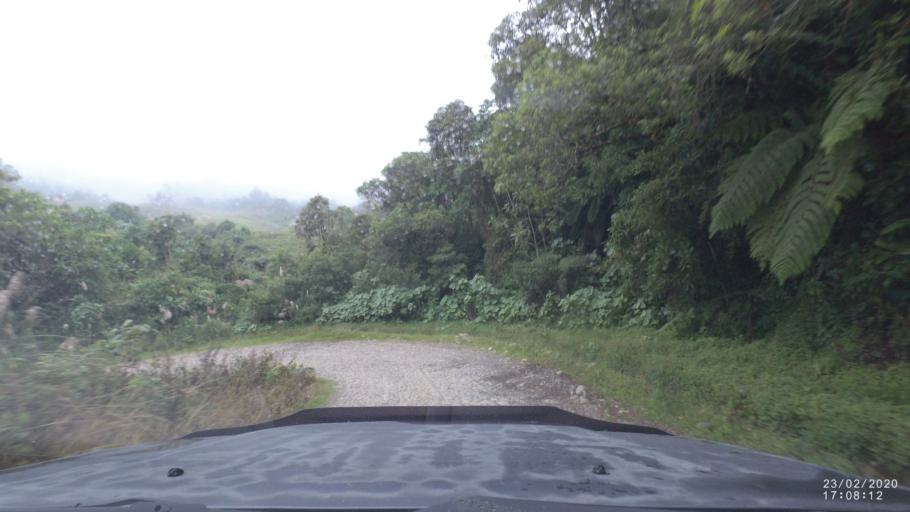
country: BO
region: Cochabamba
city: Colomi
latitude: -17.1316
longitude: -65.9569
